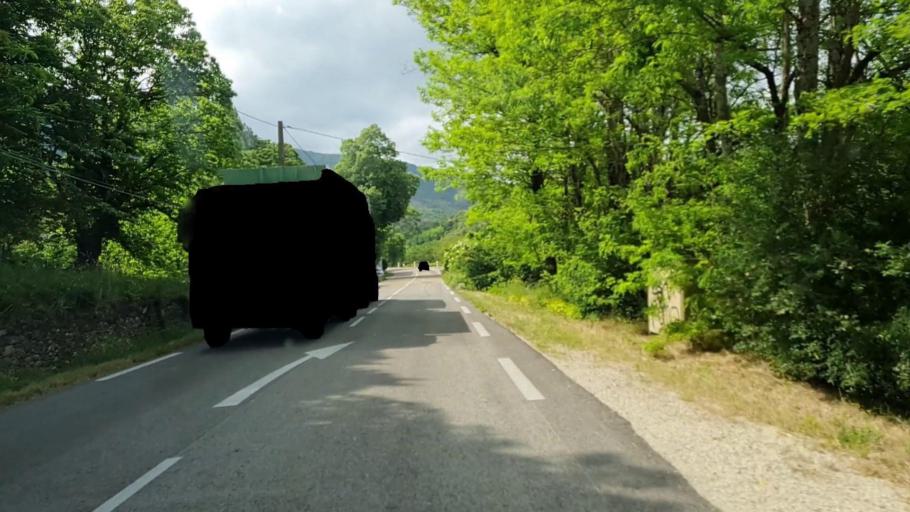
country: FR
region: Languedoc-Roussillon
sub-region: Departement du Gard
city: Sumene
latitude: 43.9749
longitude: 3.6866
